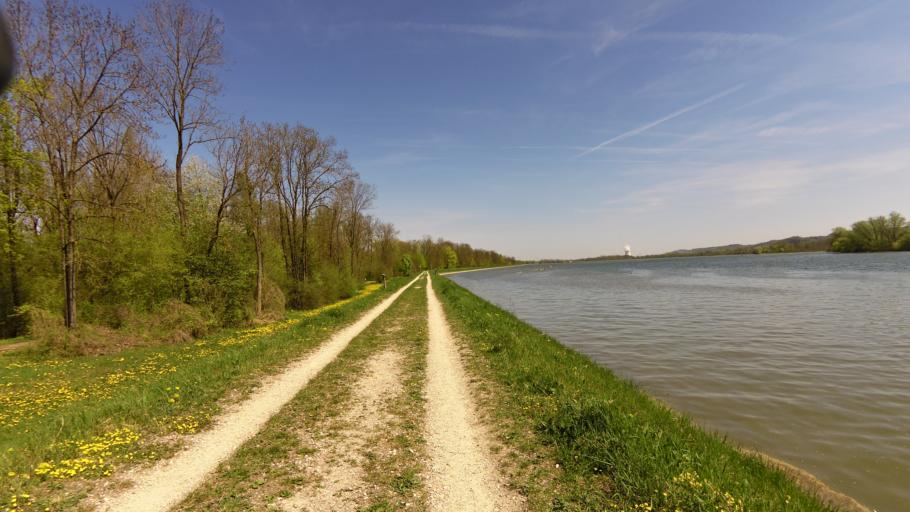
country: DE
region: Bavaria
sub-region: Lower Bavaria
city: Ergolding
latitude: 48.5685
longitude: 12.1891
